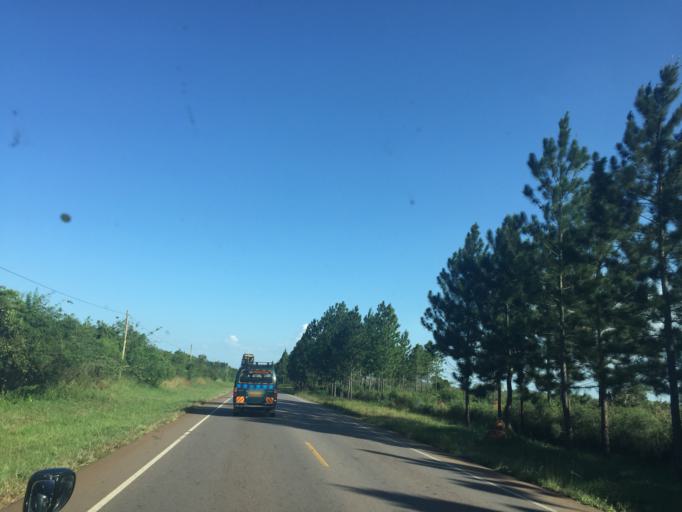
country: UG
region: Central Region
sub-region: Nakasongola District
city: Nakasongola
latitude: 1.3827
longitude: 32.3357
